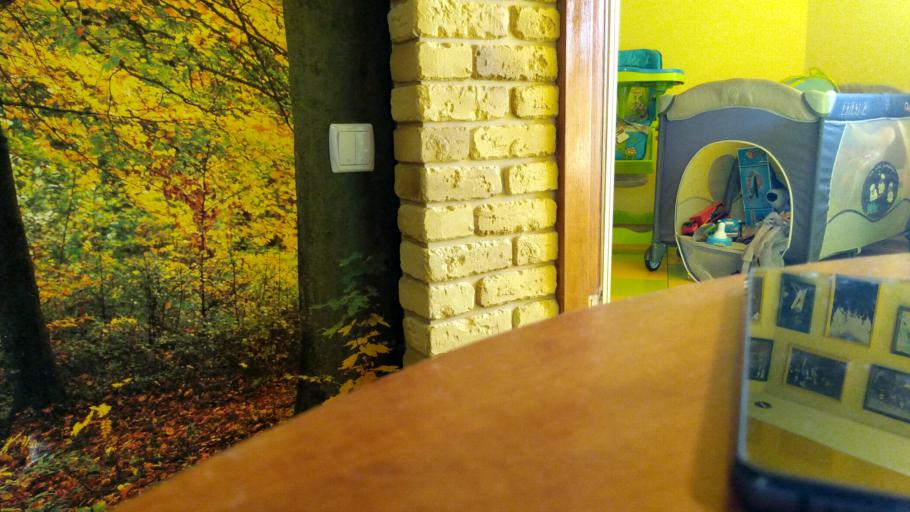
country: RU
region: Tverskaya
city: Kalashnikovo
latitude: 57.2767
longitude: 35.3802
